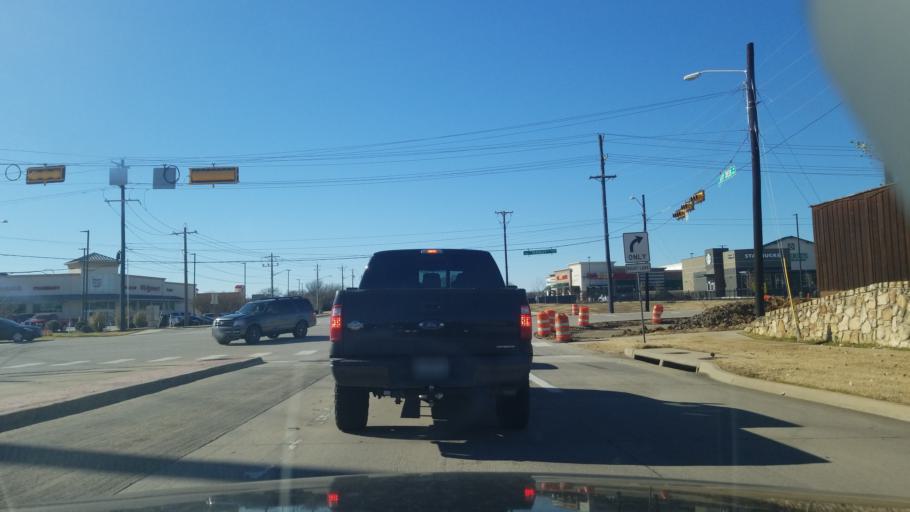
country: US
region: Texas
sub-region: Denton County
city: Corinth
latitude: 33.1472
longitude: -97.1048
